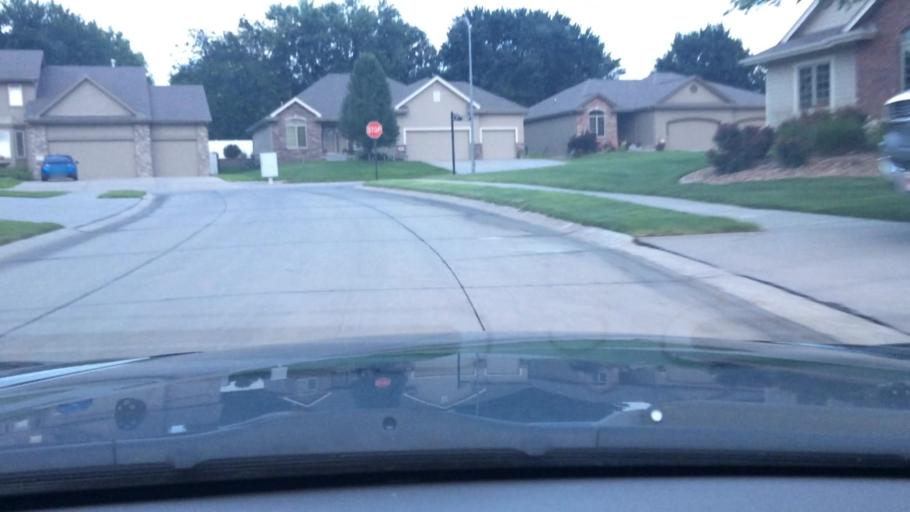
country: US
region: Nebraska
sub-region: Douglas County
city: Ralston
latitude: 41.1850
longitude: -96.0583
